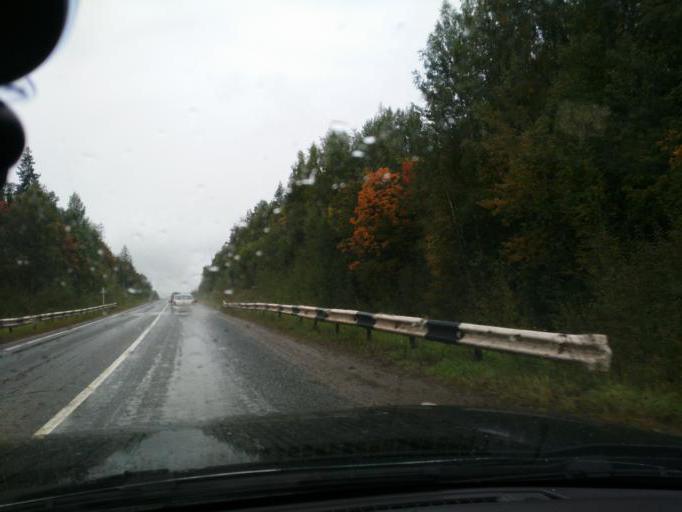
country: RU
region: Perm
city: Yugo-Kamskiy
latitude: 57.6062
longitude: 55.6539
